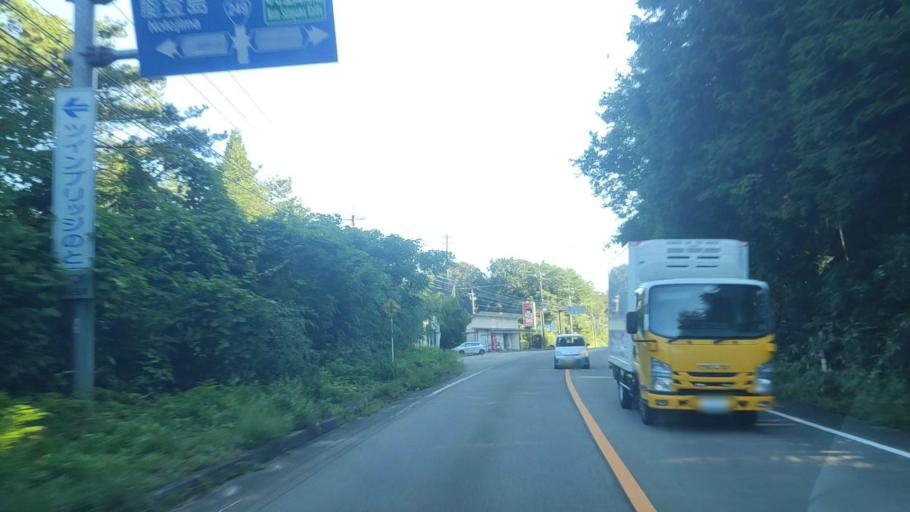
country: JP
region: Ishikawa
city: Nanao
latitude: 37.1322
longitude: 136.8637
